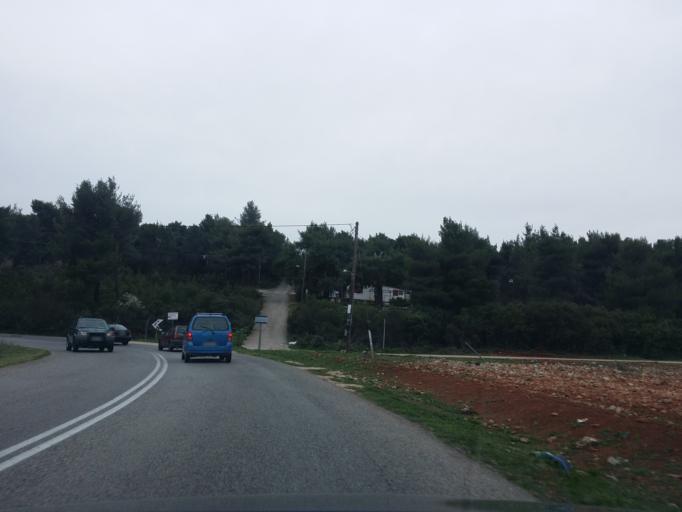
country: GR
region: Attica
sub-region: Nomarchia Dytikis Attikis
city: Vilia
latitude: 38.1278
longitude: 23.4106
